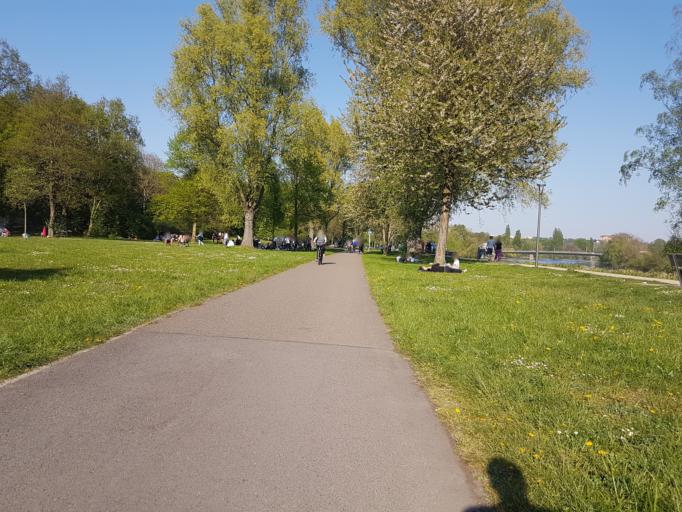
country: DE
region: North Rhine-Westphalia
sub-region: Regierungsbezirk Dusseldorf
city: Essen
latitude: 51.4426
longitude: 7.0695
